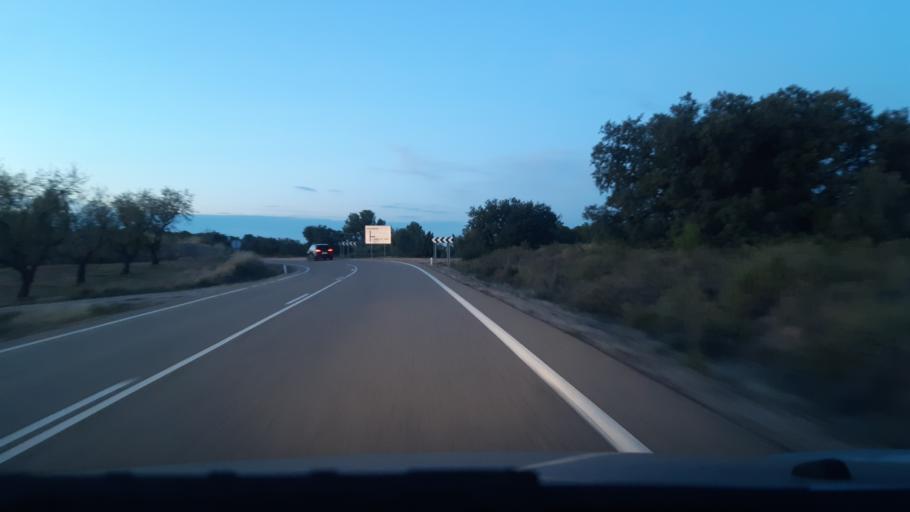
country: ES
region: Aragon
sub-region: Provincia de Teruel
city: Calaceite
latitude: 40.9757
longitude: 0.2039
